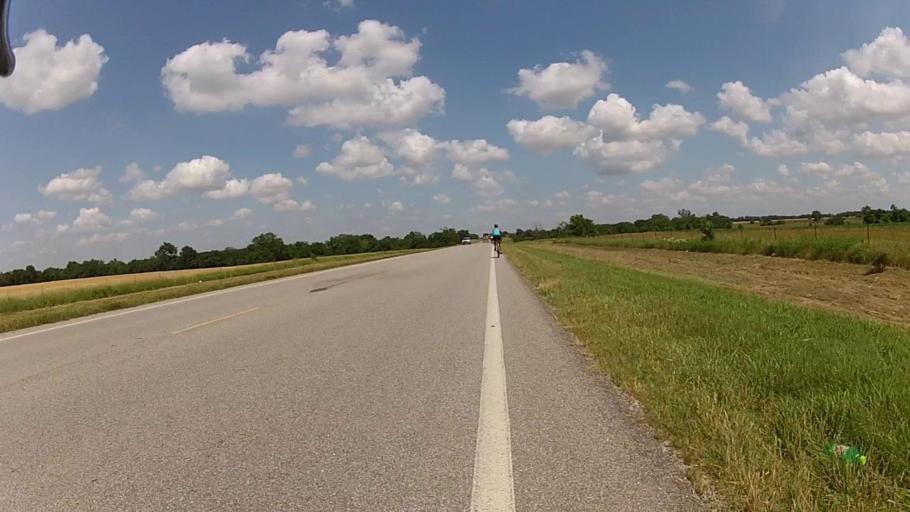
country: US
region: Kansas
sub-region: Labette County
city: Altamont
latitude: 37.1931
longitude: -95.2274
